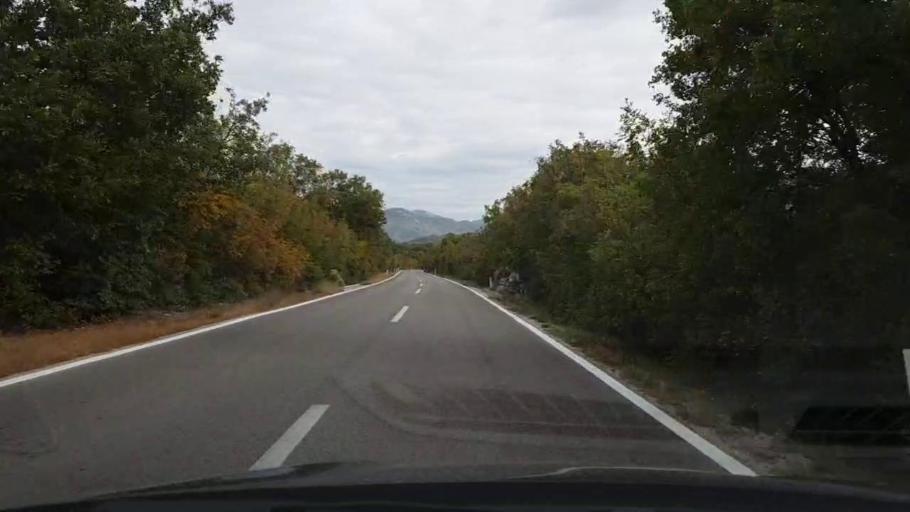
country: BA
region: Republika Srpska
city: Trebinje
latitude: 42.6878
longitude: 18.2803
